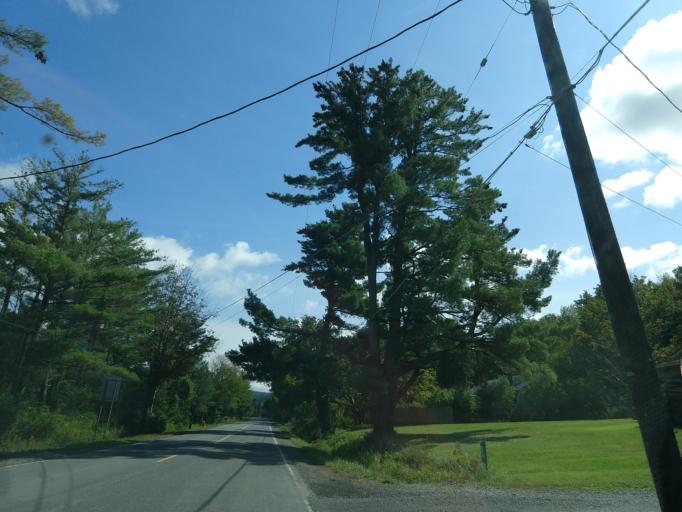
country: US
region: New York
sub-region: Tompkins County
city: East Ithaca
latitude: 42.4096
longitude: -76.4712
